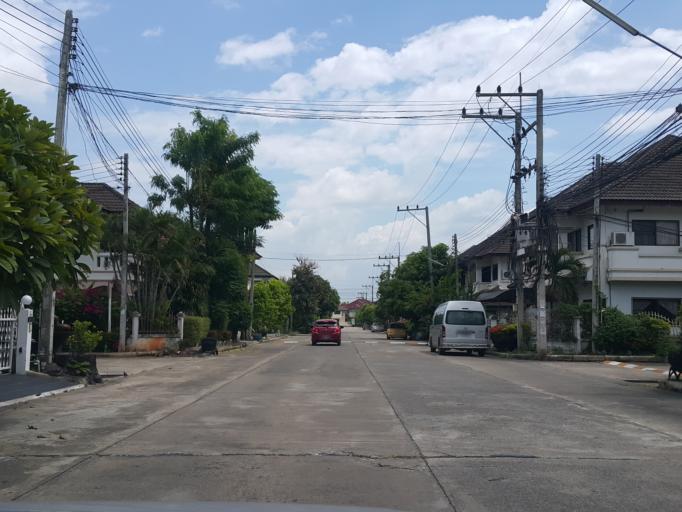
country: TH
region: Chiang Mai
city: Hang Dong
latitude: 18.7392
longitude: 98.9442
